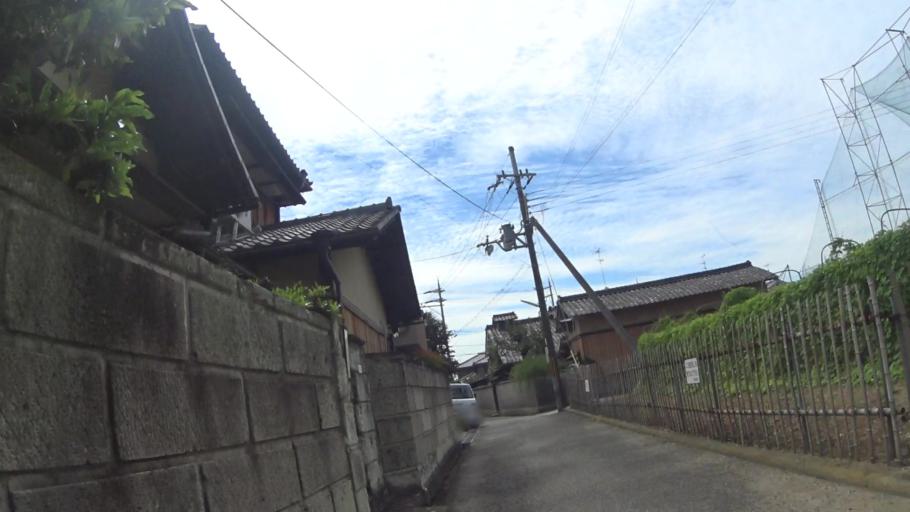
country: JP
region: Kyoto
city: Muko
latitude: 34.9477
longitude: 135.7071
